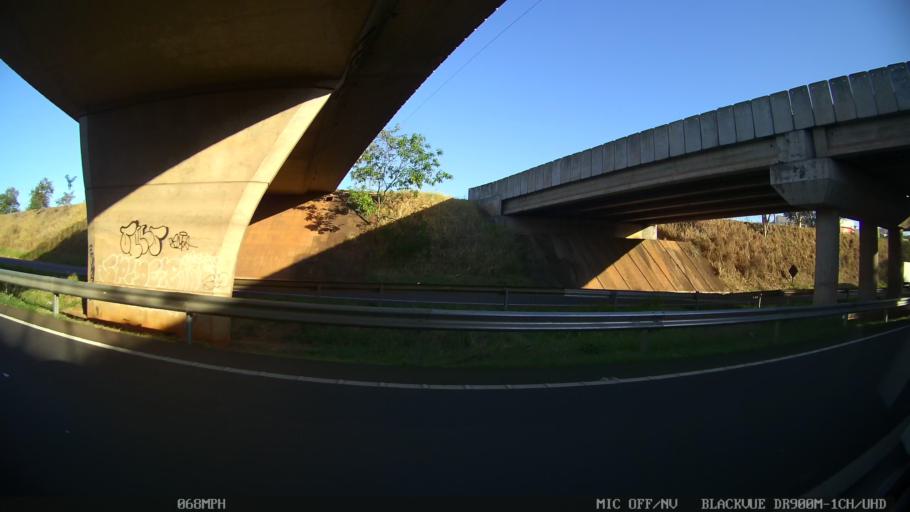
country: BR
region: Sao Paulo
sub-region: Sao Jose Do Rio Preto
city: Sao Jose do Rio Preto
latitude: -20.8014
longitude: -49.3468
